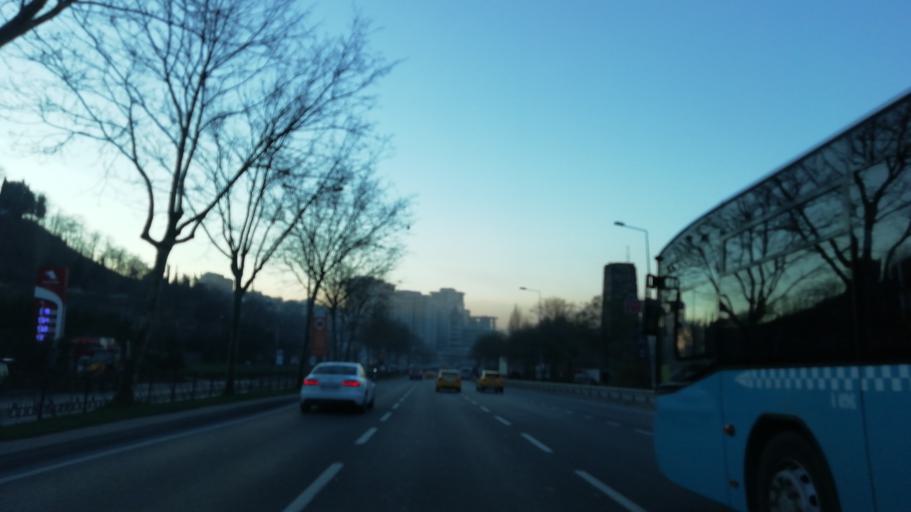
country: TR
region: Istanbul
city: Sisli
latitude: 41.0479
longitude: 28.9680
